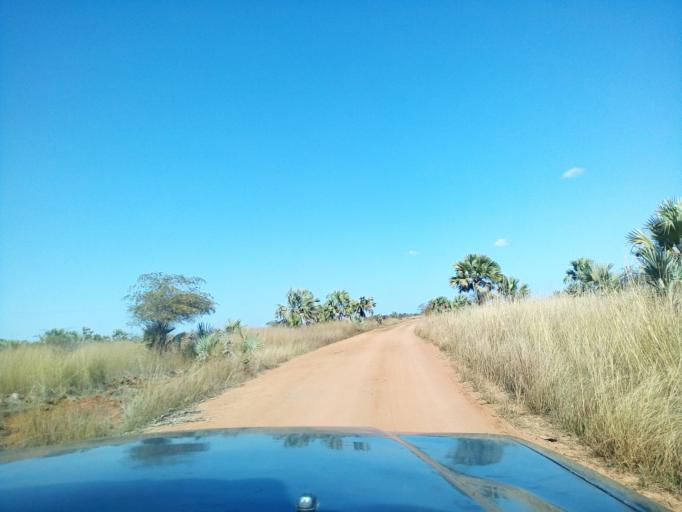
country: MG
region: Boeny
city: Mahajanga
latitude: -15.8300
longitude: 46.1670
